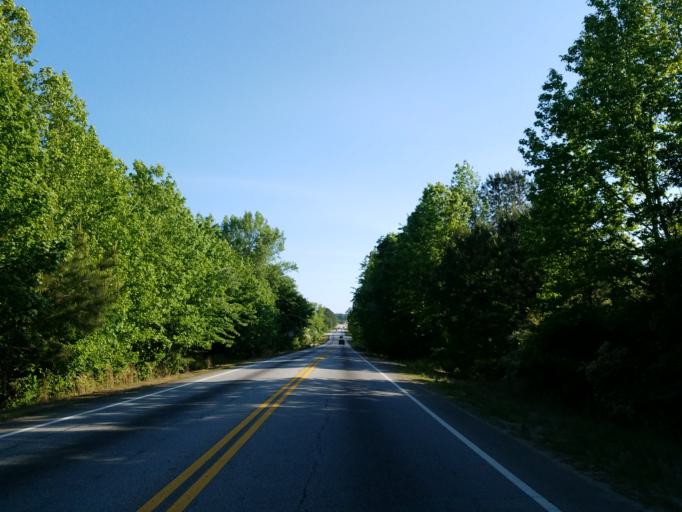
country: US
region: Georgia
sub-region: Carroll County
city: Villa Rica
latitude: 33.7391
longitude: -84.9375
